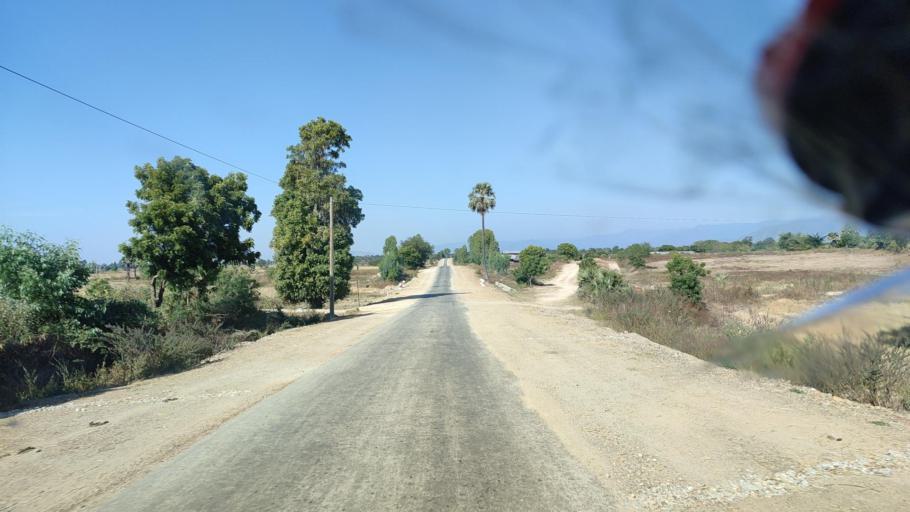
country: MM
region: Mandalay
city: Pyinmana
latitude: 20.0892
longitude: 96.2643
